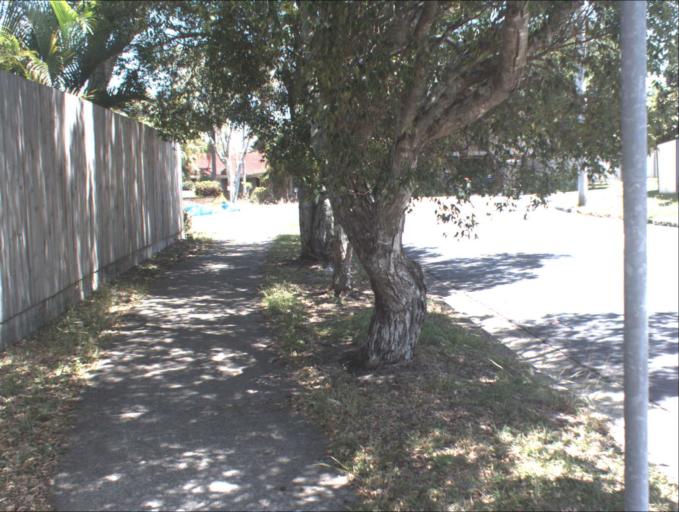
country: AU
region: Queensland
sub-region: Logan
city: Rochedale South
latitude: -27.6045
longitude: 153.1149
